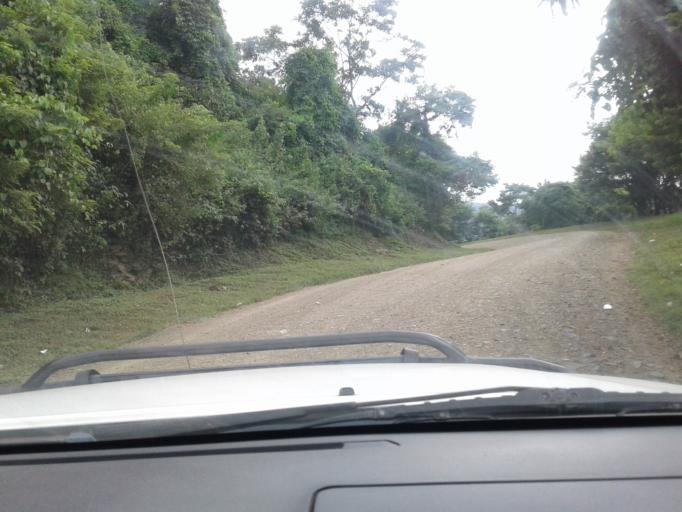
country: NI
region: Matagalpa
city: San Ramon
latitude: 12.9035
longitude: -85.8012
